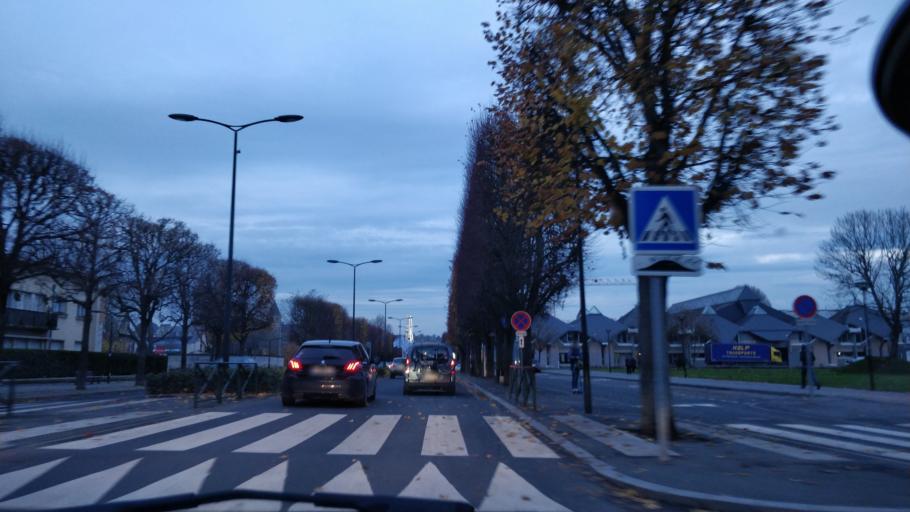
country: FR
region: Lower Normandy
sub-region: Departement du Calvados
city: Caen
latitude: 49.1761
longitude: -0.3711
